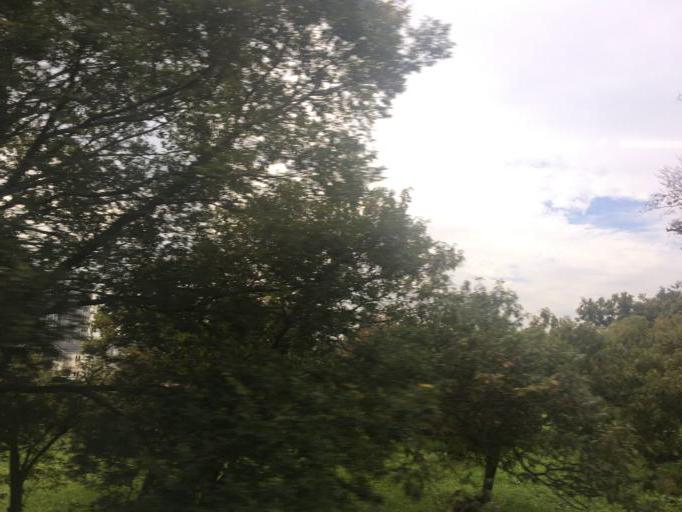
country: JP
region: Tokyo
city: Hino
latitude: 35.7027
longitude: 139.3611
